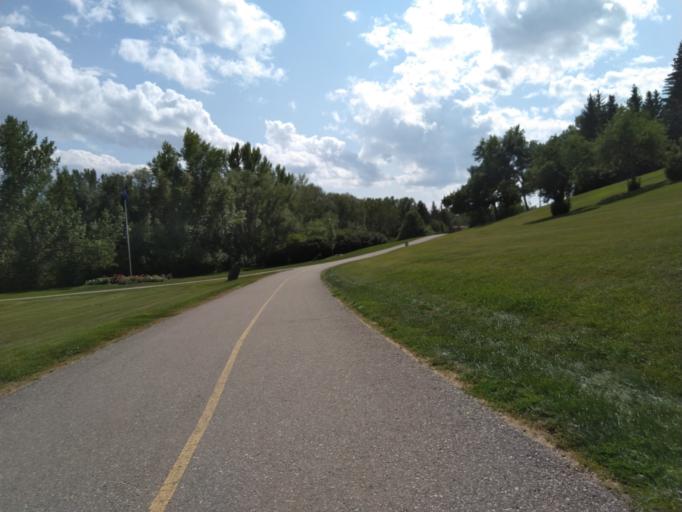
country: CA
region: Alberta
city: Calgary
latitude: 51.0781
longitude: -114.0820
